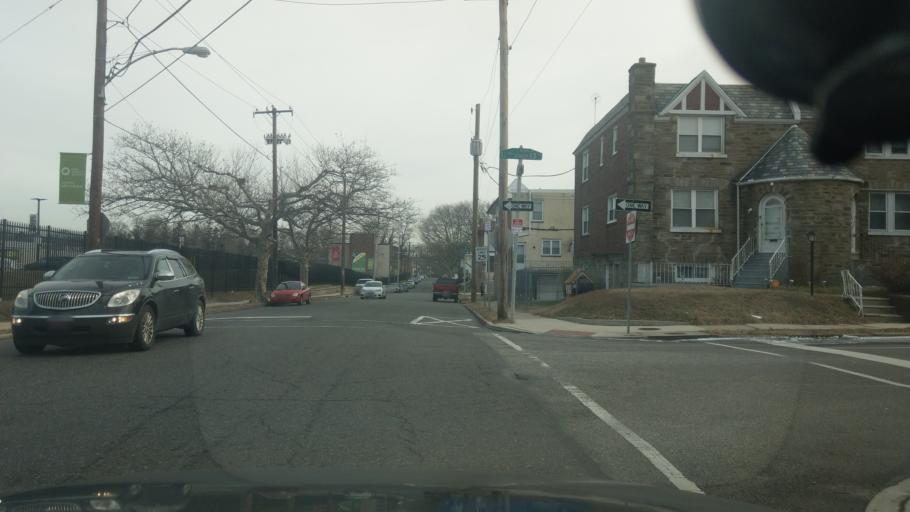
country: US
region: Pennsylvania
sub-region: Montgomery County
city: Wyncote
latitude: 40.0457
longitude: -75.1413
